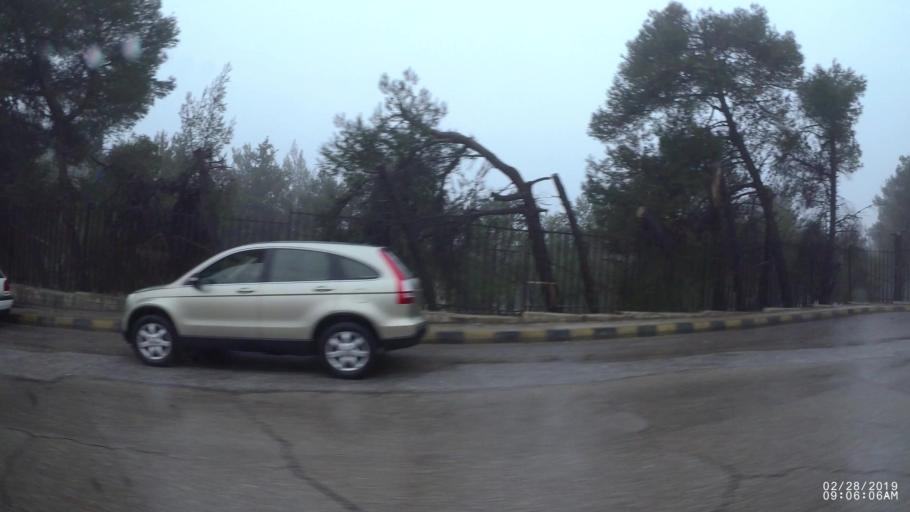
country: JO
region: Amman
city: Al Jubayhah
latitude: 32.0173
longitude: 35.8750
